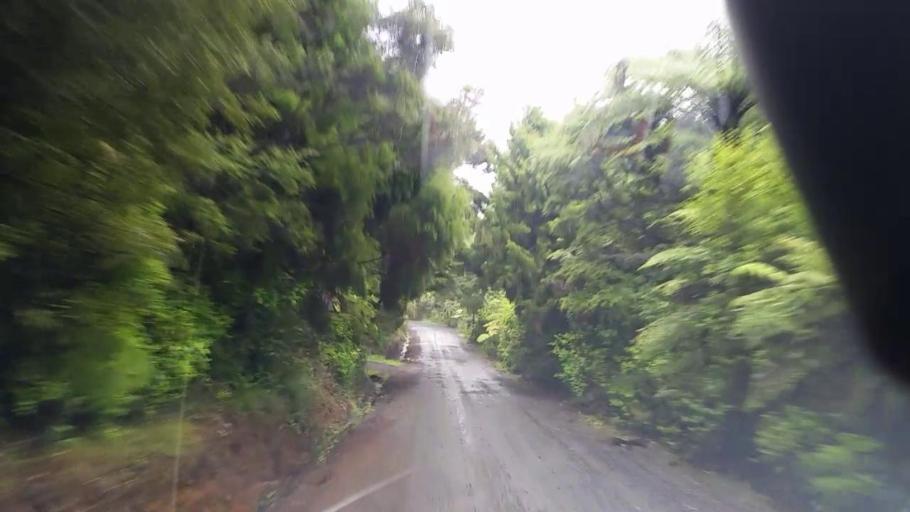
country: NZ
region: Auckland
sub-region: Auckland
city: Muriwai Beach
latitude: -36.8720
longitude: 174.5098
